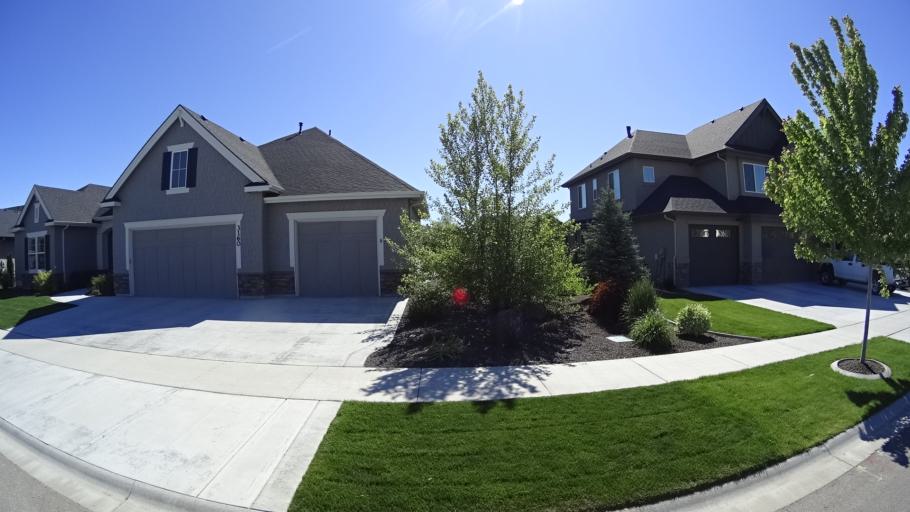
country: US
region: Idaho
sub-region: Ada County
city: Eagle
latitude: 43.6664
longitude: -116.3979
